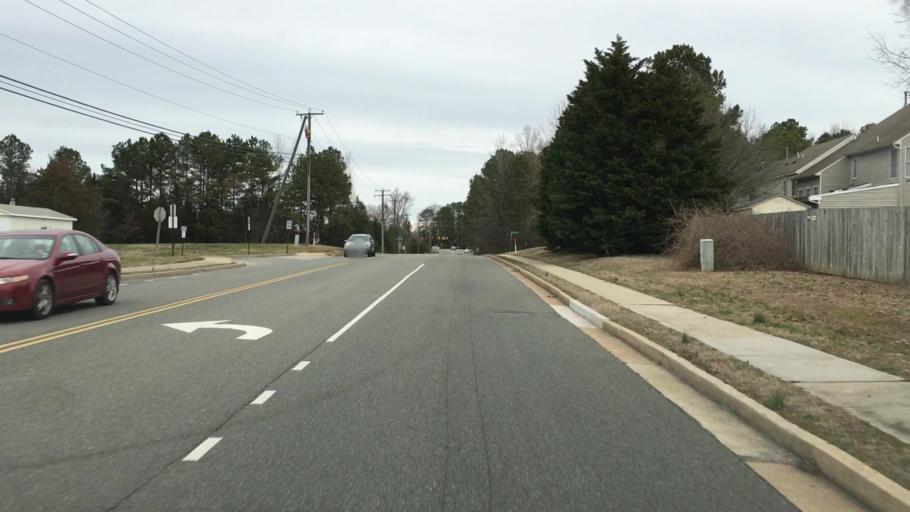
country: US
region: Virginia
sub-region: Henrico County
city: Glen Allen
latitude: 37.6673
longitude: -77.5427
